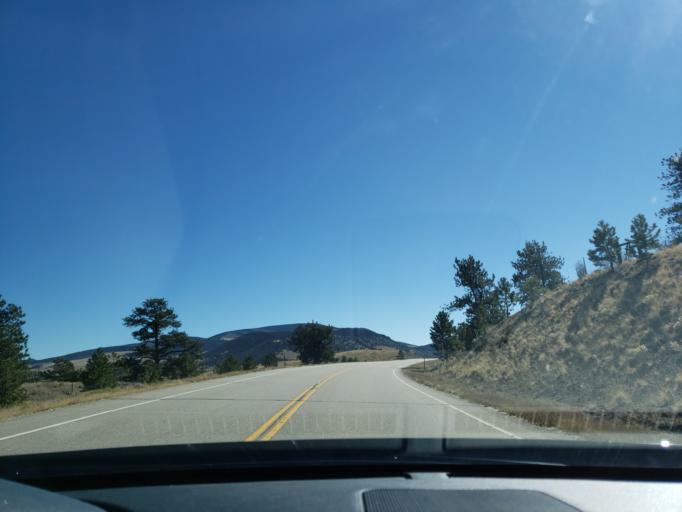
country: US
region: Colorado
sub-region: Chaffee County
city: Buena Vista
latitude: 38.8774
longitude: -105.6745
